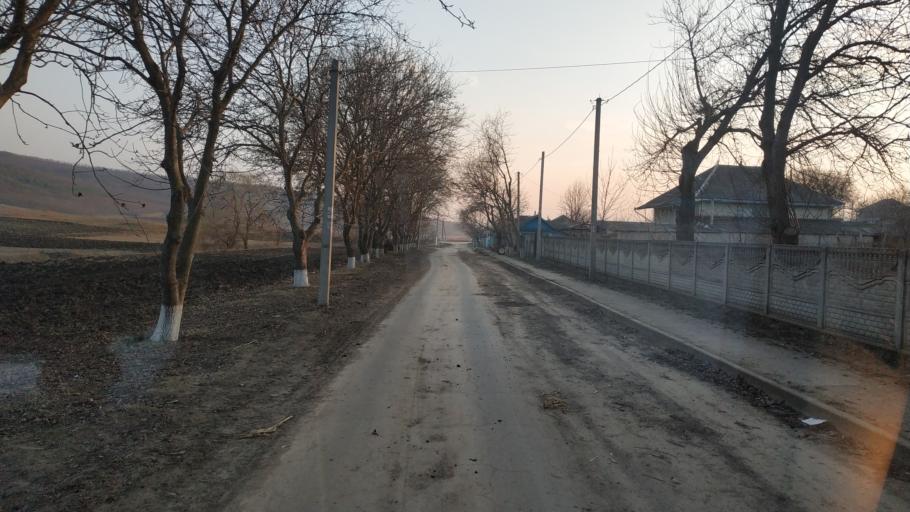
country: MD
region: Hincesti
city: Dancu
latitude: 46.7067
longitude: 28.3451
